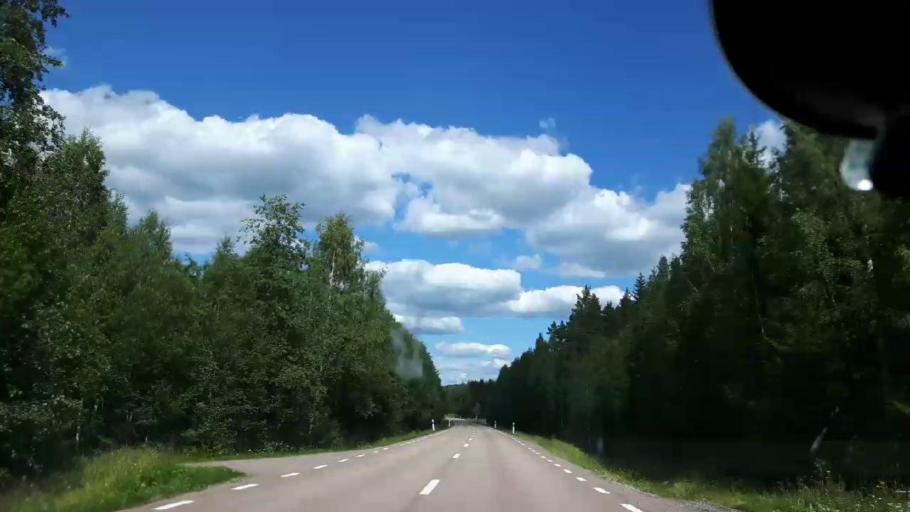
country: SE
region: Jaemtland
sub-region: Ragunda Kommun
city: Hammarstrand
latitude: 62.9037
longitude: 16.7004
